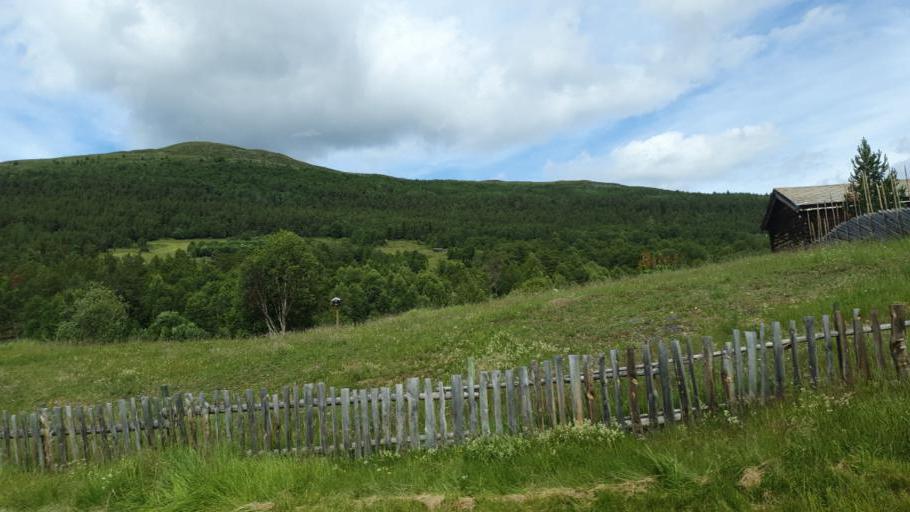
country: NO
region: Oppland
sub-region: Vaga
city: Vagamo
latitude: 61.7285
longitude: 9.0734
